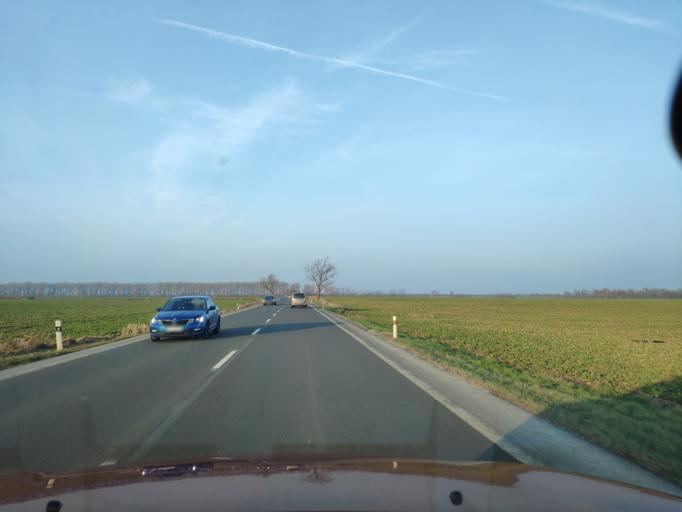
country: SK
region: Trnavsky
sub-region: Okres Trnava
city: Trnava
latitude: 48.3204
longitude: 17.5145
